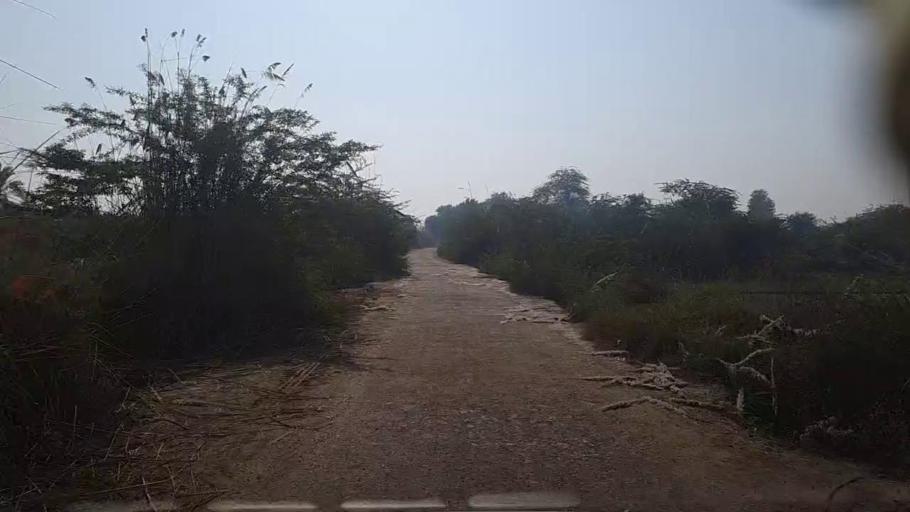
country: PK
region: Sindh
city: Kandiari
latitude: 26.9792
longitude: 68.4694
